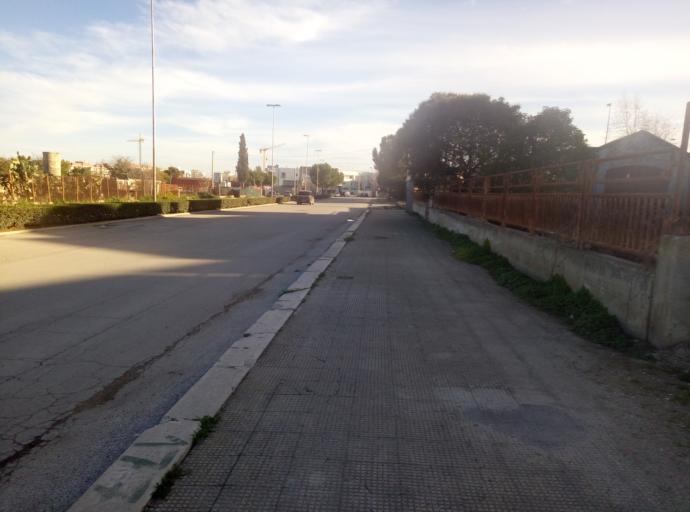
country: IT
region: Apulia
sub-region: Provincia di Bari
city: Ruvo di Puglia
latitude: 41.1183
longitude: 16.4920
